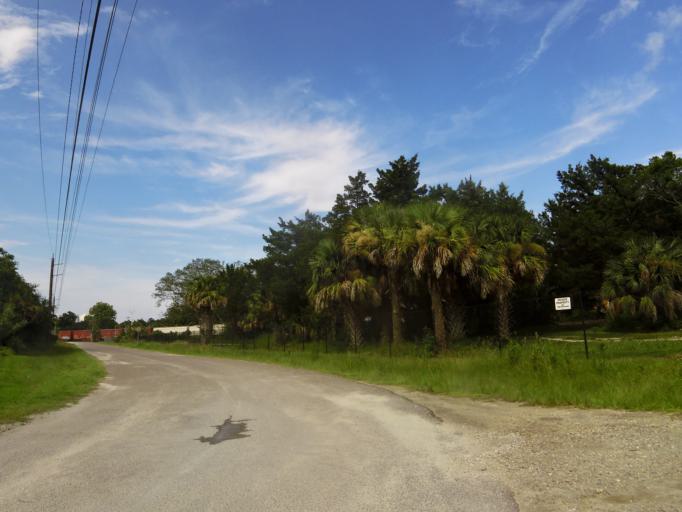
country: US
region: Florida
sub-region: Nassau County
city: Fernandina Beach
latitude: 30.6670
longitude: -81.4665
